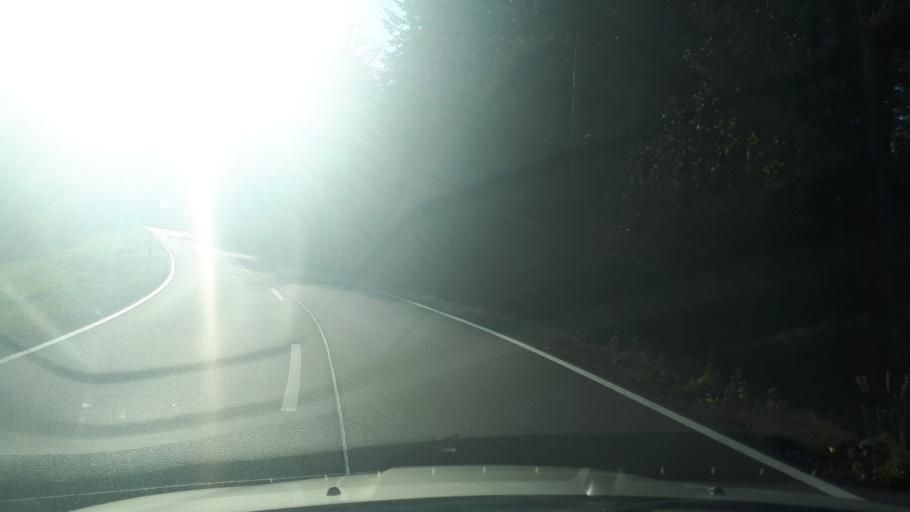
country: DE
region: Rheinland-Pfalz
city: Kliding
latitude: 50.1424
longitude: 7.0515
